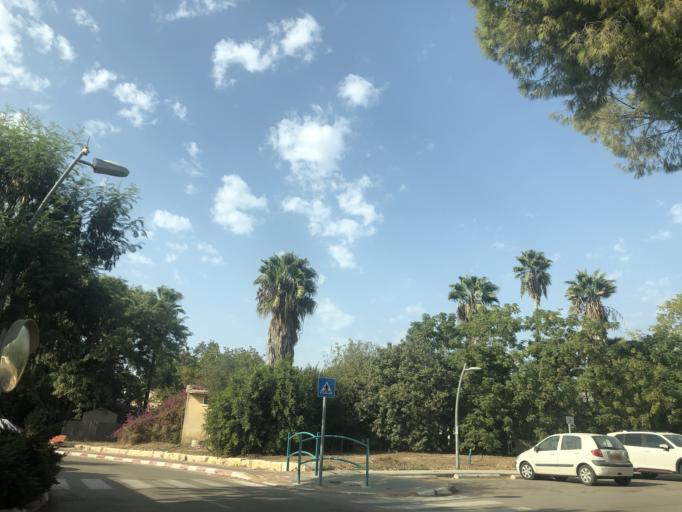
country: IL
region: Central District
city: Rosh Ha'Ayin
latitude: 32.0826
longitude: 34.9354
